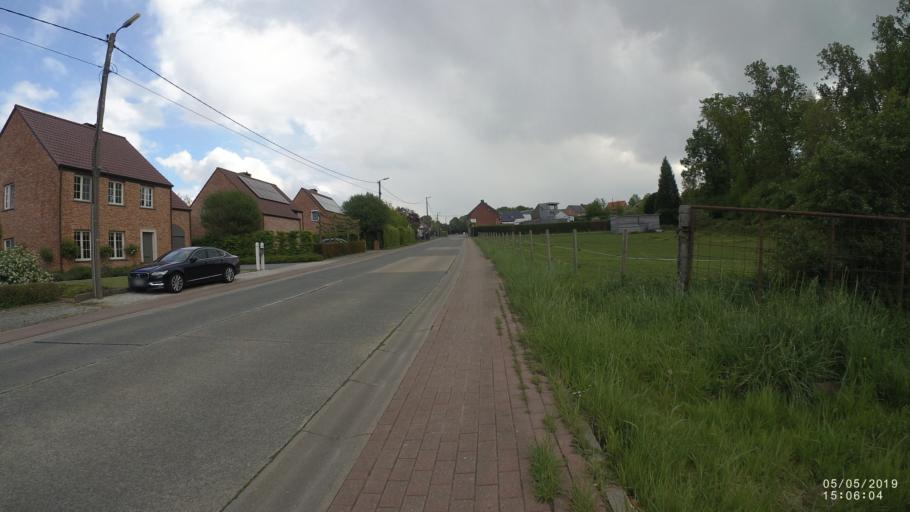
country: BE
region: Flanders
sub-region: Provincie Vlaams-Brabant
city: Lubbeek
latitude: 50.8783
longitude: 4.8777
